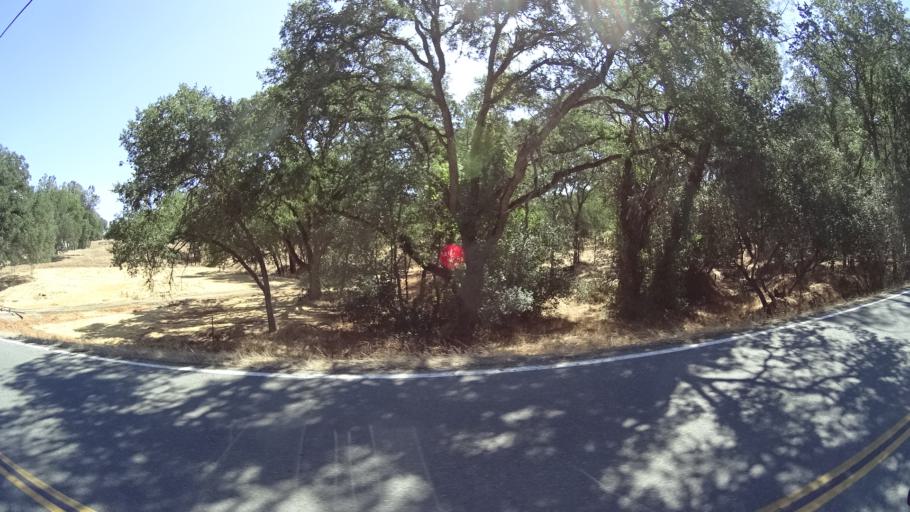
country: US
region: California
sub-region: Calaveras County
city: Valley Springs
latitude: 38.2132
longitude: -120.8790
